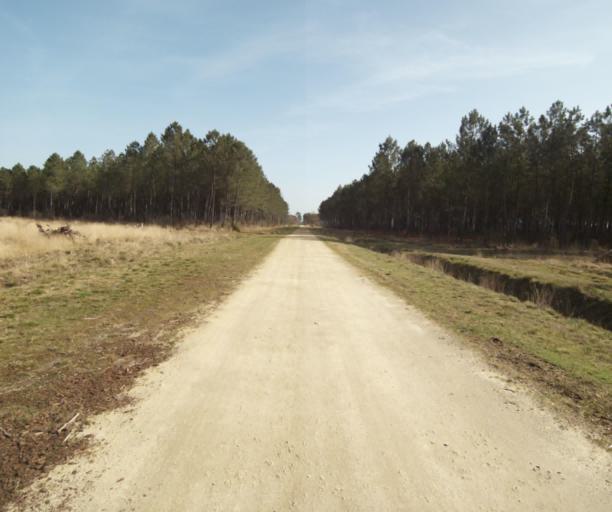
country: FR
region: Aquitaine
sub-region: Departement de la Gironde
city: Bazas
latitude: 44.2260
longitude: -0.2376
